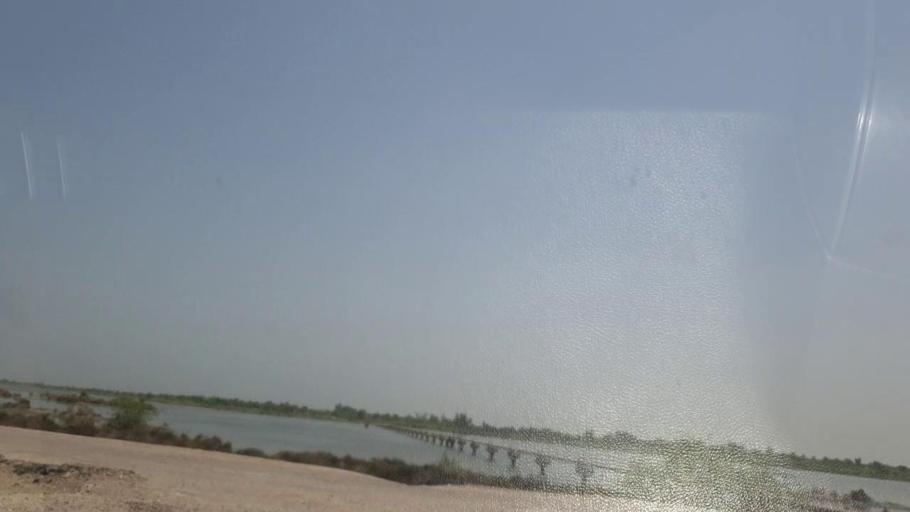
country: PK
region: Sindh
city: Kot Diji
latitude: 27.2903
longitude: 68.6456
